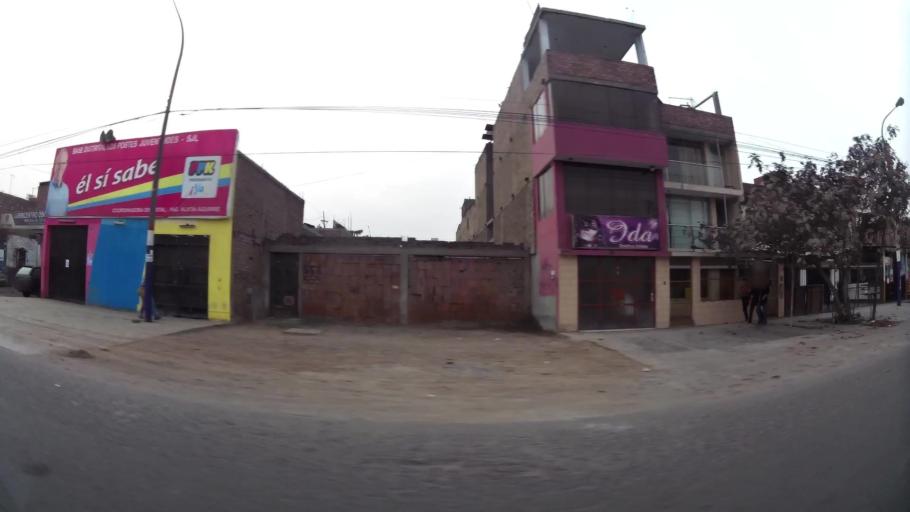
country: PE
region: Lima
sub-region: Lima
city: Independencia
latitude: -11.9961
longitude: -77.0036
